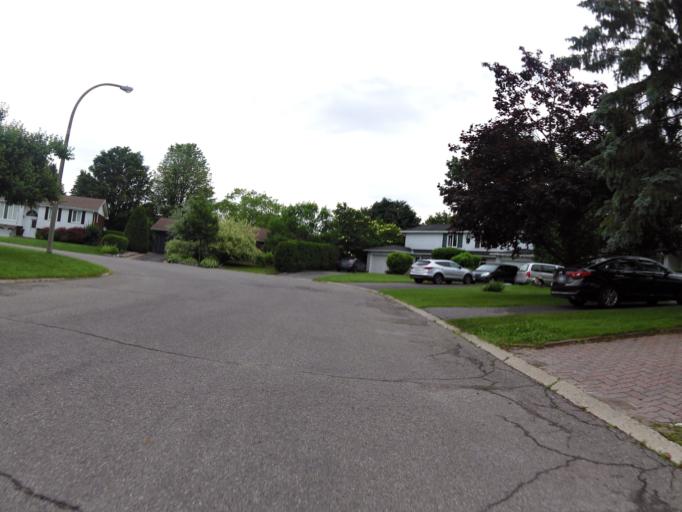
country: CA
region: Ontario
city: Bells Corners
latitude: 45.3352
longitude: -75.7774
